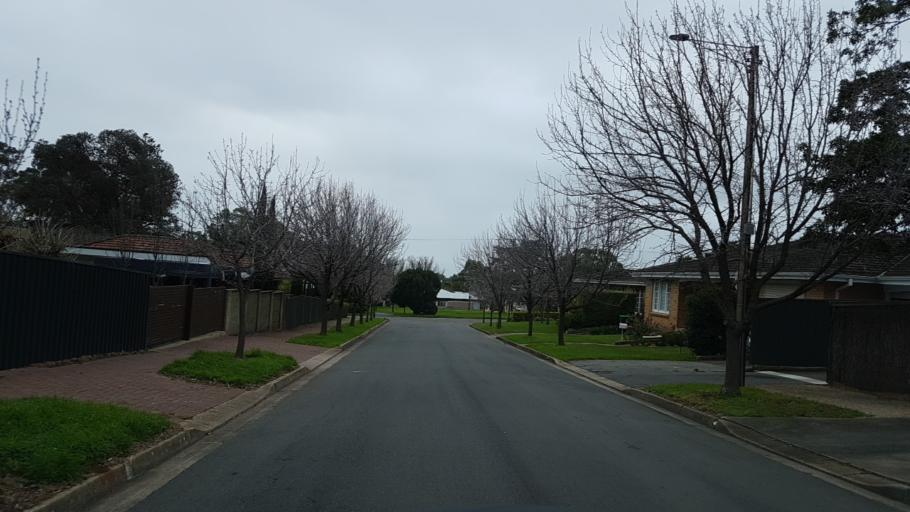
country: AU
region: South Australia
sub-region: Burnside
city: Linden Park
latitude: -34.9446
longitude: 138.6538
